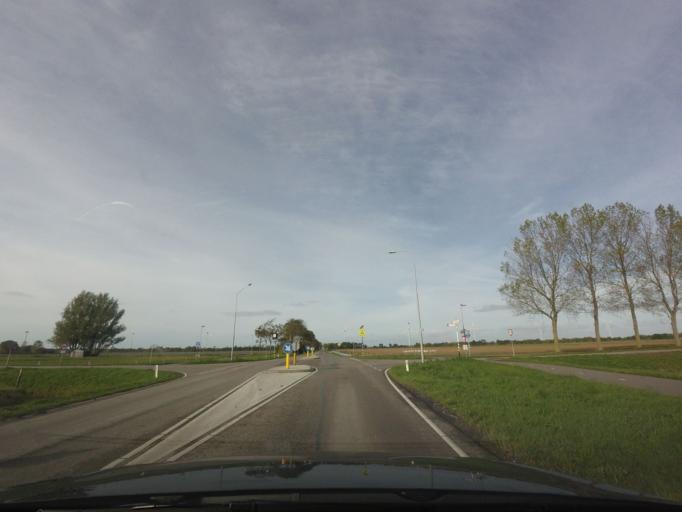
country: NL
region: North Holland
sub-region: Gemeente Schagen
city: Harenkarspel
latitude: 52.7181
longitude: 4.7867
